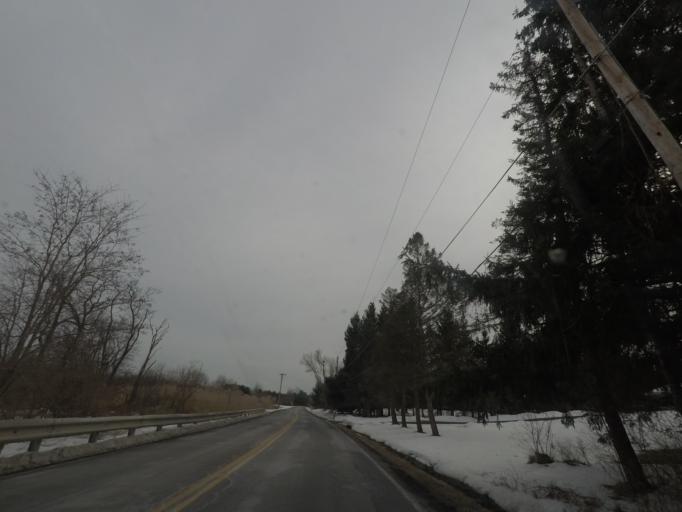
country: US
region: New York
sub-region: Albany County
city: Altamont
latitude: 42.6875
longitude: -73.9842
